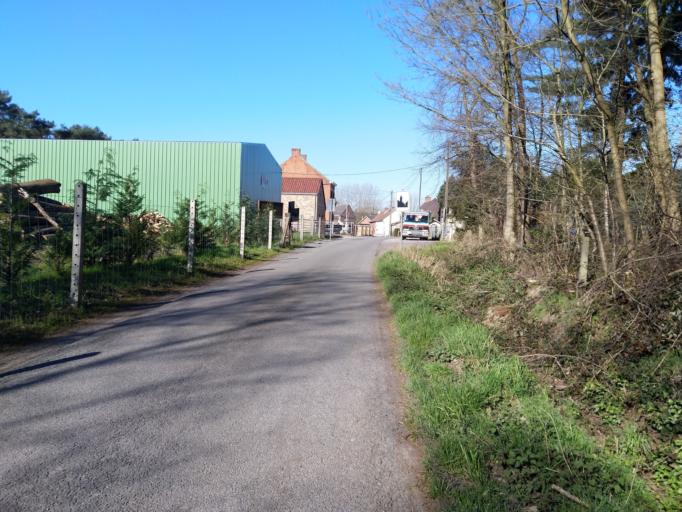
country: BE
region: Wallonia
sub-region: Province du Hainaut
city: Jurbise
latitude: 50.5063
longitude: 3.8776
